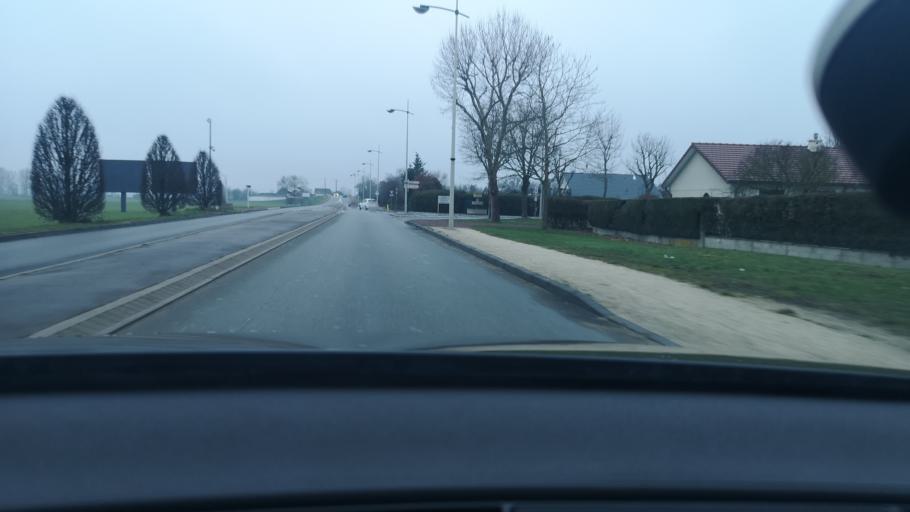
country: FR
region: Bourgogne
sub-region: Departement de la Cote-d'Or
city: Longvic
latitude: 47.2799
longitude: 5.0626
